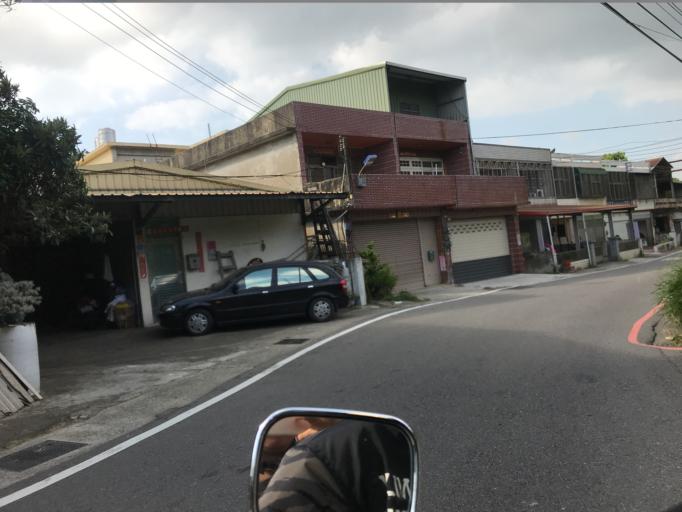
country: TW
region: Taiwan
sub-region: Hsinchu
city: Hsinchu
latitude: 24.7794
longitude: 120.9319
